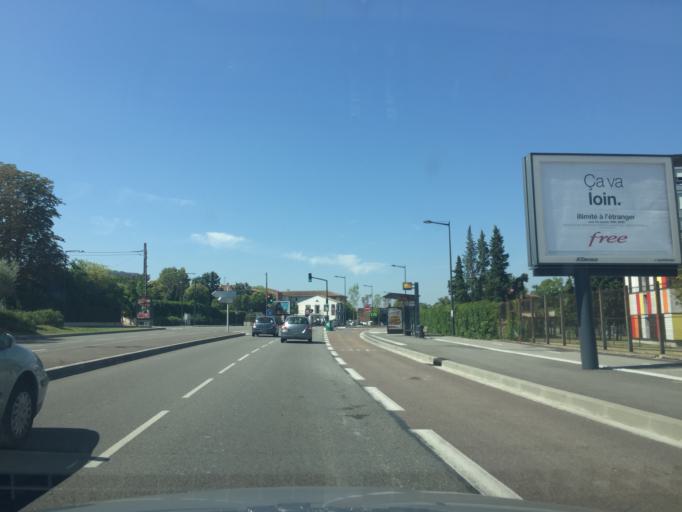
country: FR
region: Midi-Pyrenees
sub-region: Departement de la Haute-Garonne
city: Ramonville-Saint-Agne
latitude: 43.5554
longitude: 1.4669
